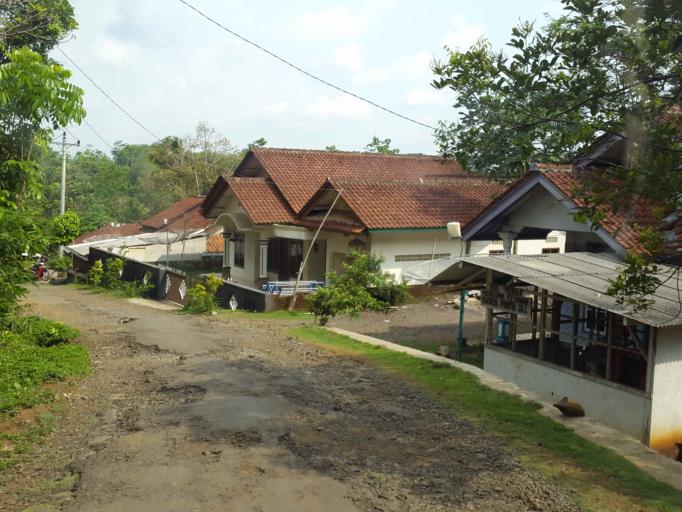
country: ID
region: Central Java
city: Cimalati
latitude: -7.3107
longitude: 108.6501
